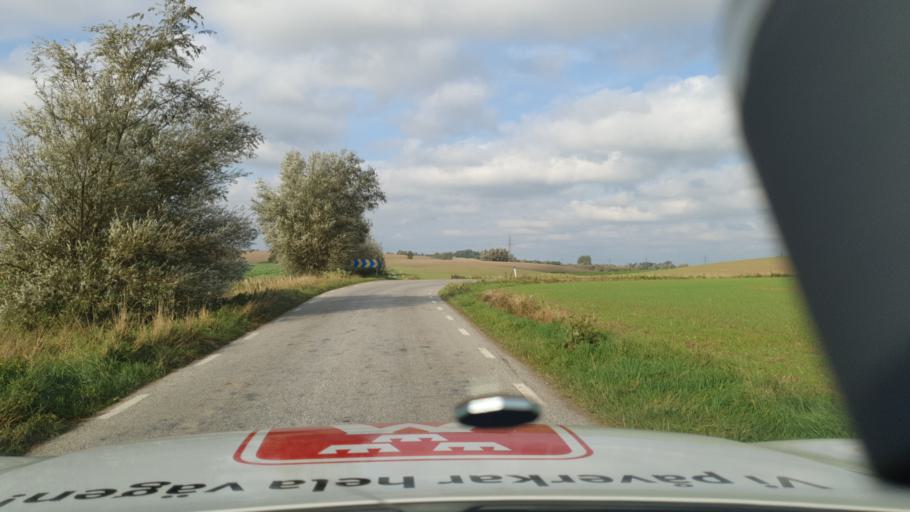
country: SE
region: Skane
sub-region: Svedala Kommun
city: Svedala
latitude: 55.4877
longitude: 13.1877
